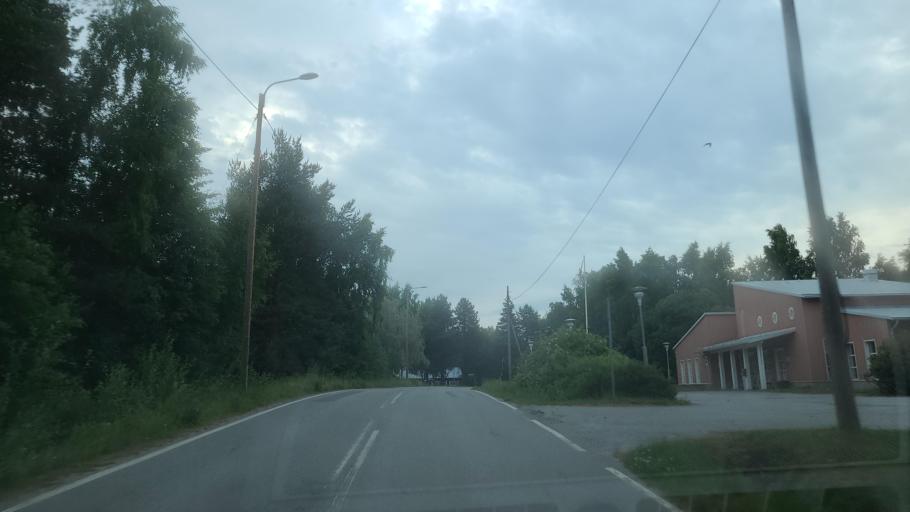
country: FI
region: Ostrobothnia
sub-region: Vaasa
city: Replot
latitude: 63.1896
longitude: 21.3008
